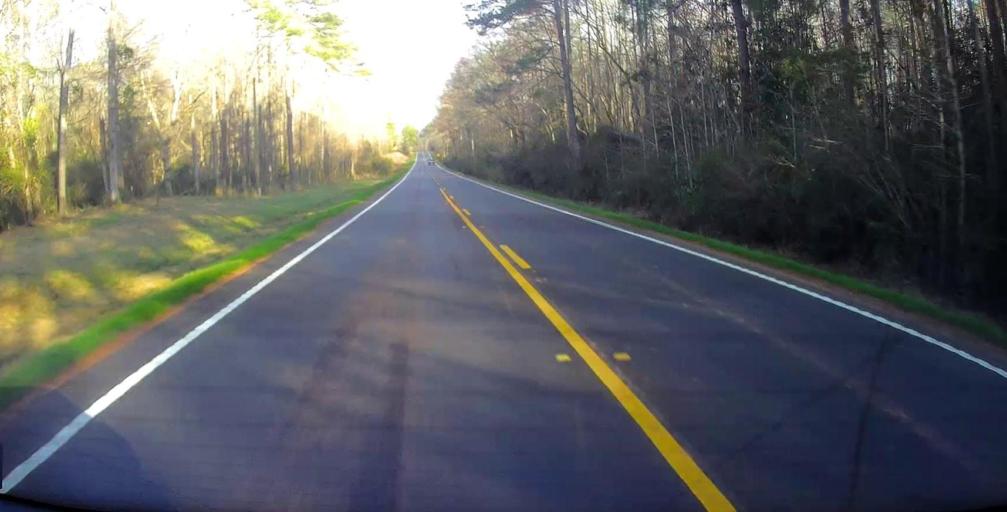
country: US
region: Georgia
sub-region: Harris County
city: Hamilton
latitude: 32.7492
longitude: -84.9203
